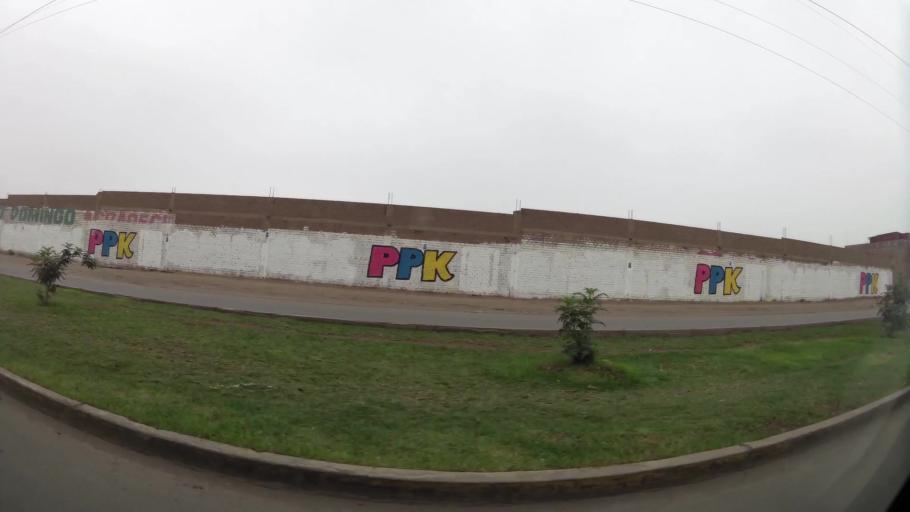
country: PE
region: Lima
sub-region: Lima
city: Urb. Santo Domingo
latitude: -11.8720
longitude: -77.0277
